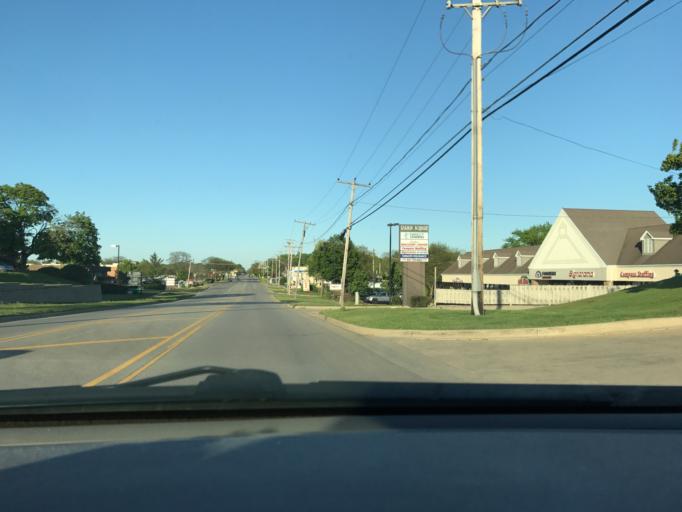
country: US
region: Illinois
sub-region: Kane County
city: Elgin
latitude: 42.0330
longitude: -88.3232
